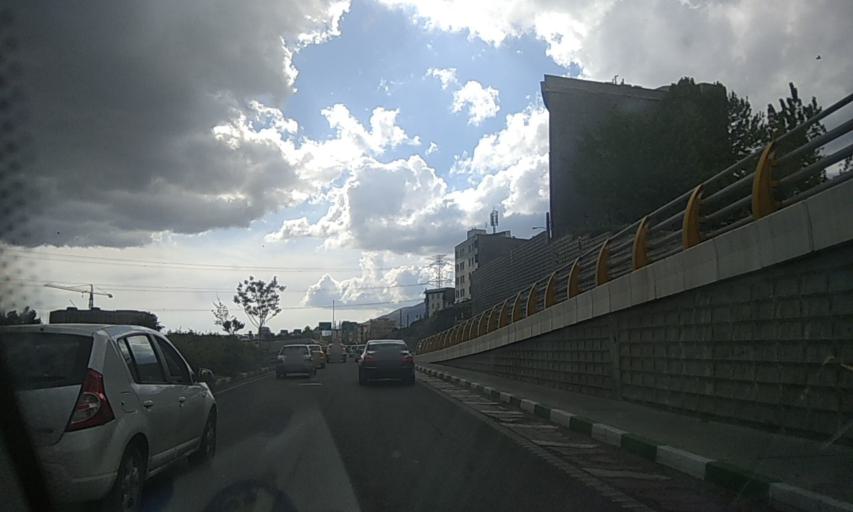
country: IR
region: Tehran
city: Tajrish
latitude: 35.7706
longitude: 51.3219
